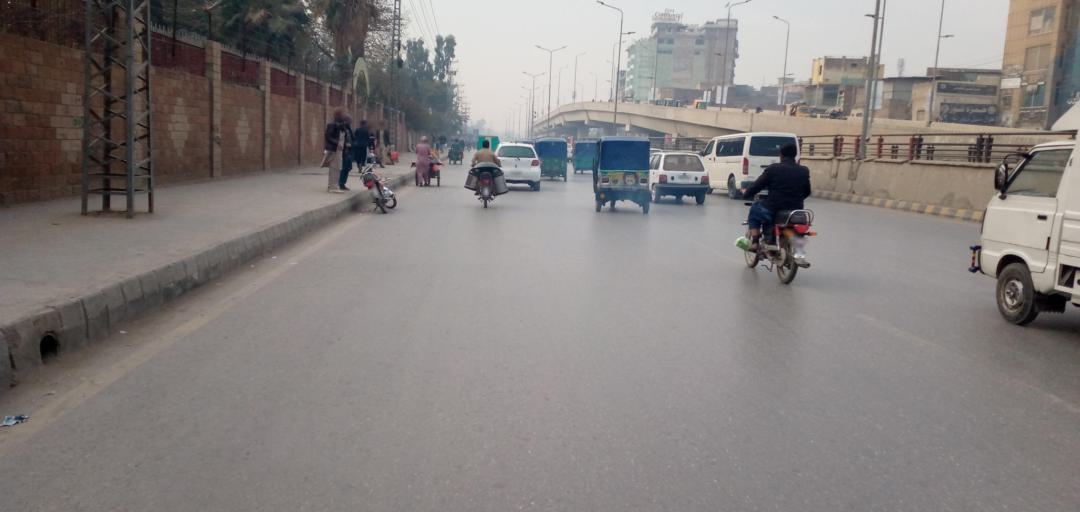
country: PK
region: Khyber Pakhtunkhwa
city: Peshawar
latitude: 34.0146
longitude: 71.5768
